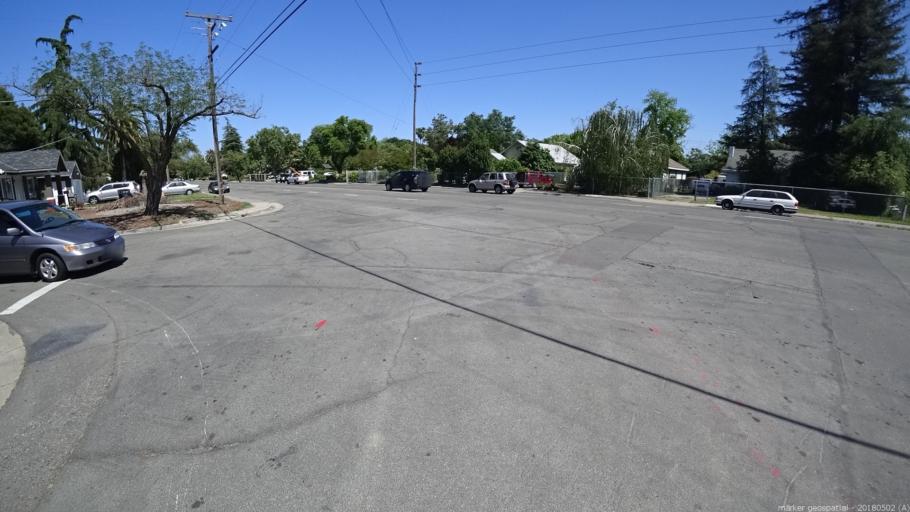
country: US
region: California
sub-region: Sacramento County
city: Arden-Arcade
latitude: 38.6238
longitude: -121.4303
